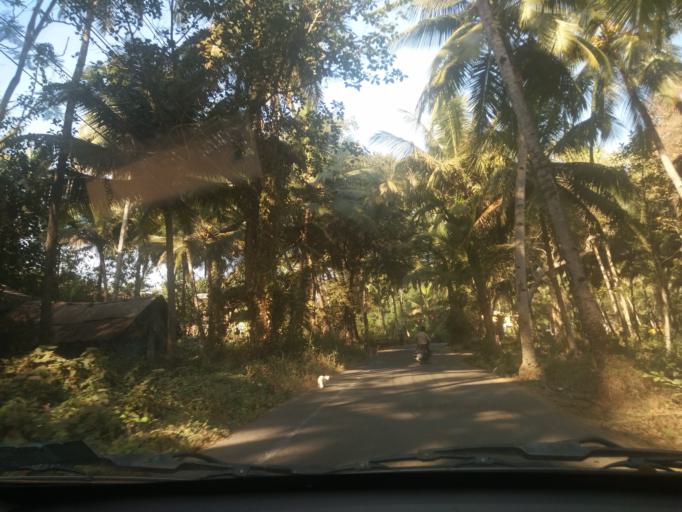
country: IN
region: Goa
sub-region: South Goa
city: Colva
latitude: 15.3023
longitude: 73.9165
